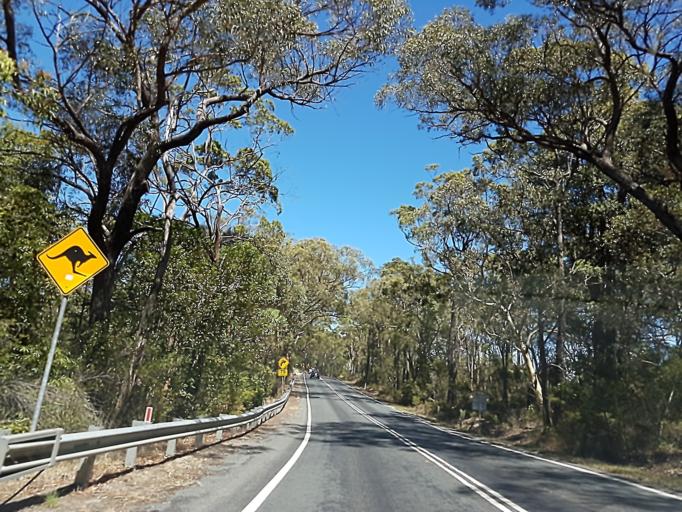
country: AU
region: New South Wales
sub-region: Hornsby Shire
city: Glenorie
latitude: -33.4911
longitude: 151.0193
